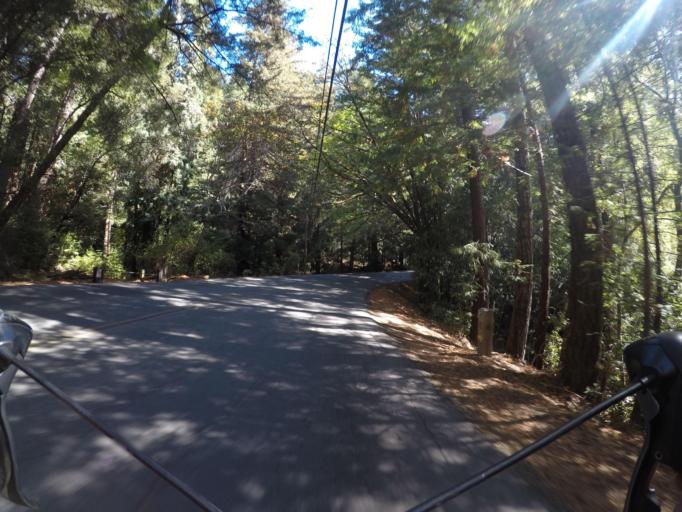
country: US
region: California
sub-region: San Mateo County
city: Portola Valley
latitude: 37.2781
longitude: -122.2951
